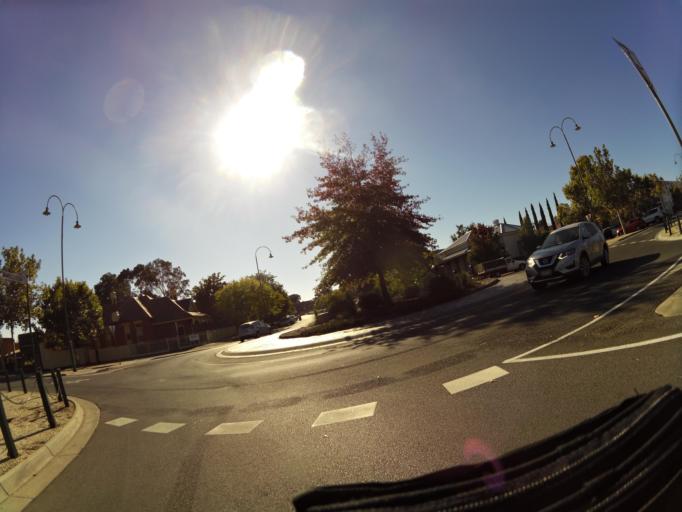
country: AU
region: Victoria
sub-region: Greater Bendigo
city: Bendigo
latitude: -36.7624
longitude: 144.2842
